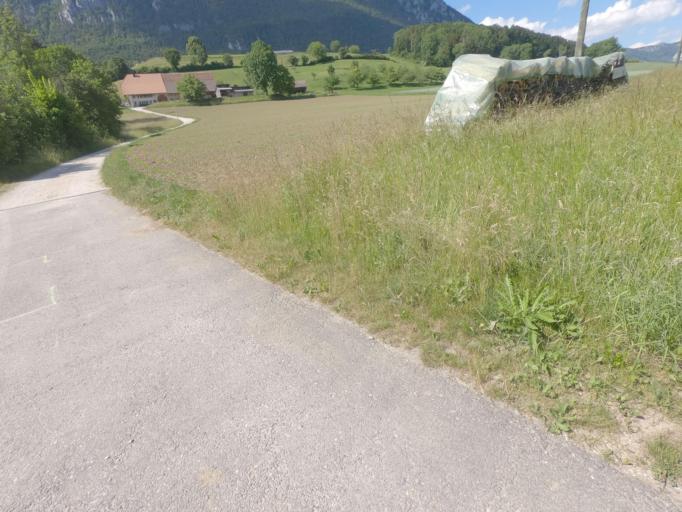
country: CH
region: Solothurn
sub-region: Bezirk Lebern
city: Langendorf
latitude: 47.2333
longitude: 7.5326
